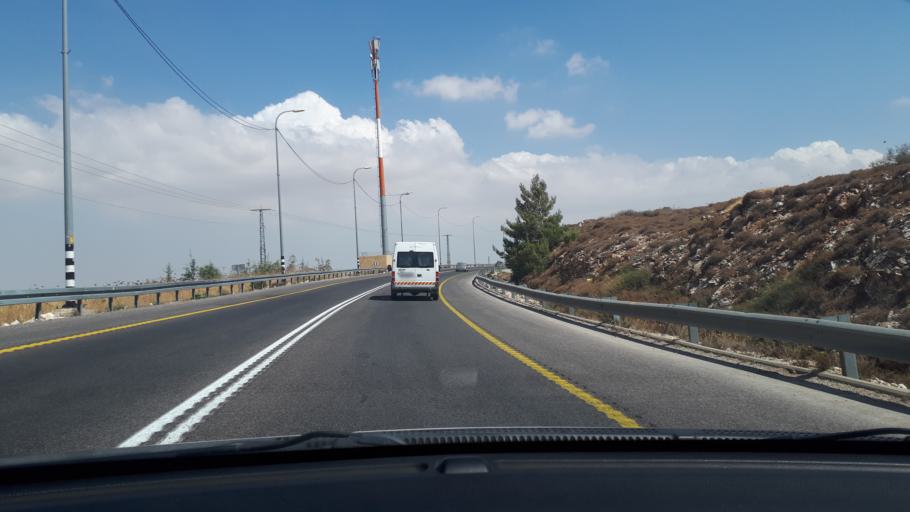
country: PS
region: West Bank
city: Mikhmas
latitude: 31.8915
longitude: 35.2754
